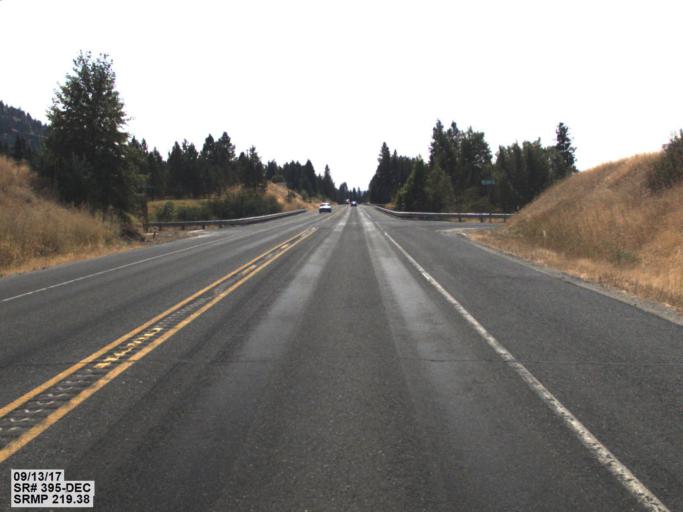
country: US
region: Washington
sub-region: Stevens County
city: Colville
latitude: 48.4072
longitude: -117.8508
